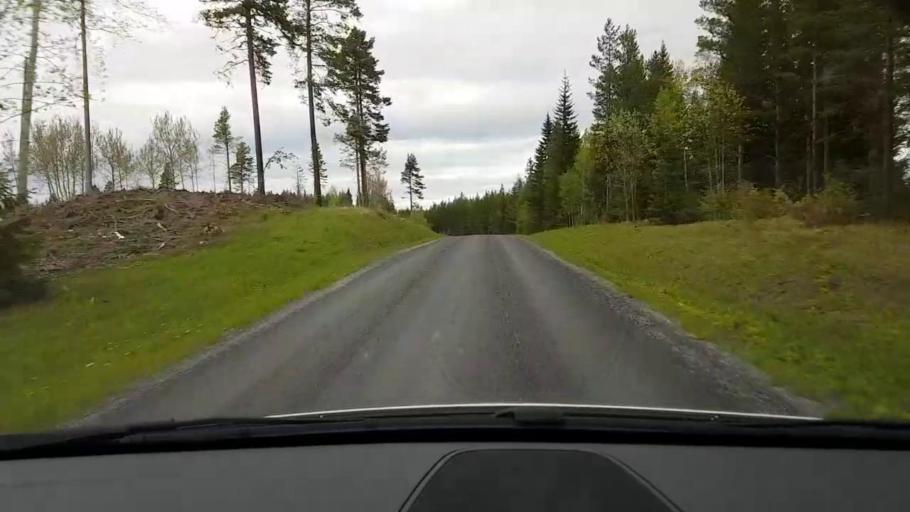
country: SE
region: Jaemtland
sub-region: Krokoms Kommun
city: Krokom
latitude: 63.3008
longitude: 14.3975
